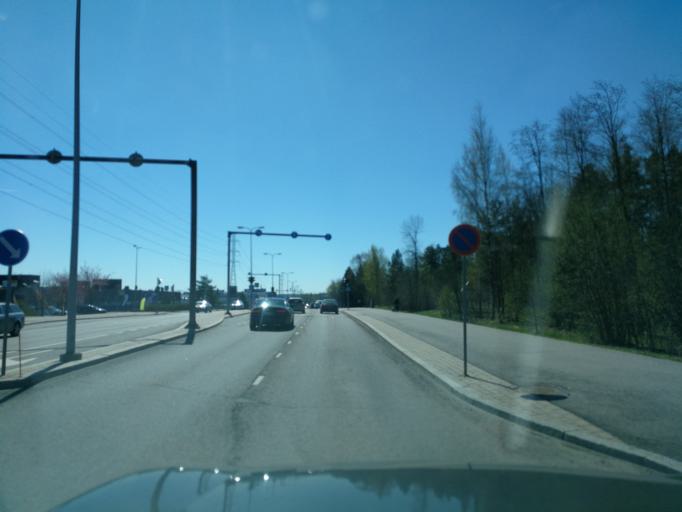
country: FI
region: Uusimaa
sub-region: Helsinki
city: Vantaa
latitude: 60.2781
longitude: 24.9704
